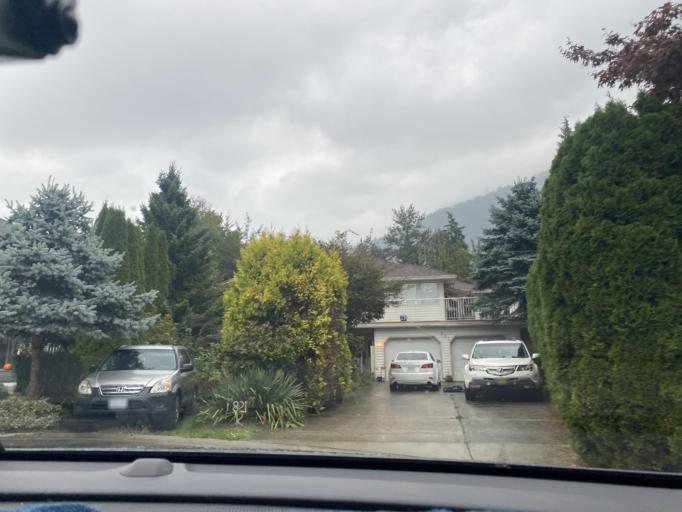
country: CA
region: British Columbia
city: Agassiz
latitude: 49.2873
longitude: -121.7782
